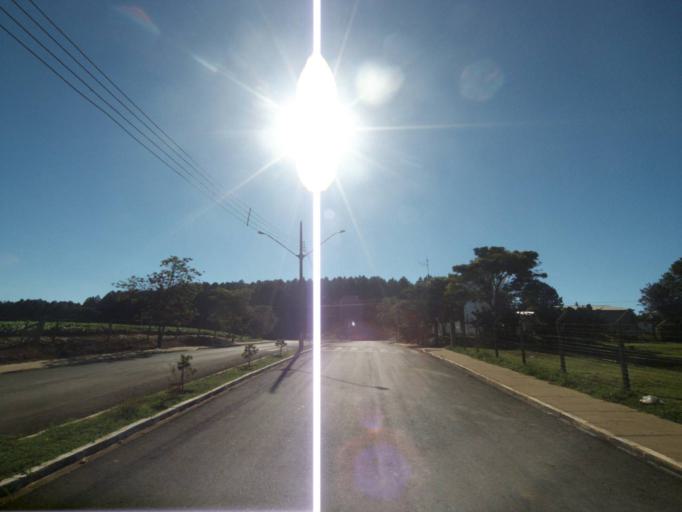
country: BR
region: Parana
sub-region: Pinhao
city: Pinhao
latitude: -25.8344
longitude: -52.0237
